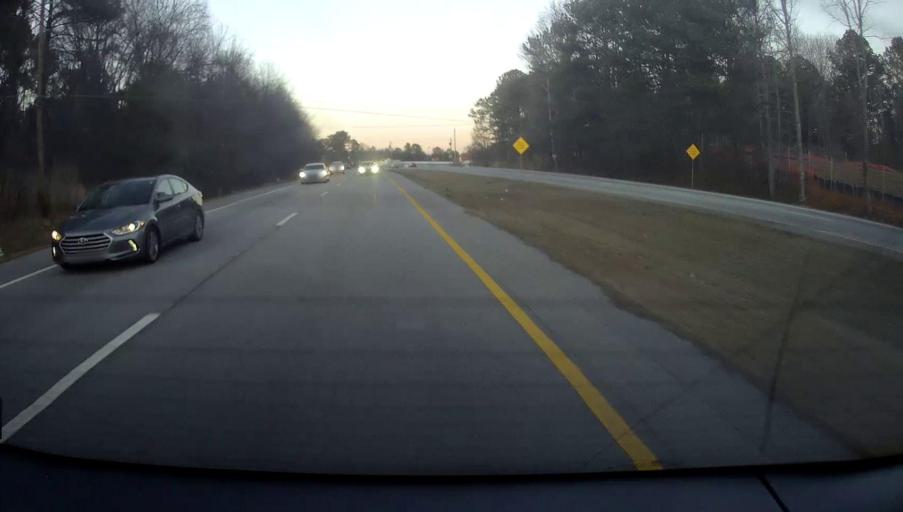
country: US
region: Georgia
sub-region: Fayette County
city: Fayetteville
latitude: 33.4994
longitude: -84.4282
